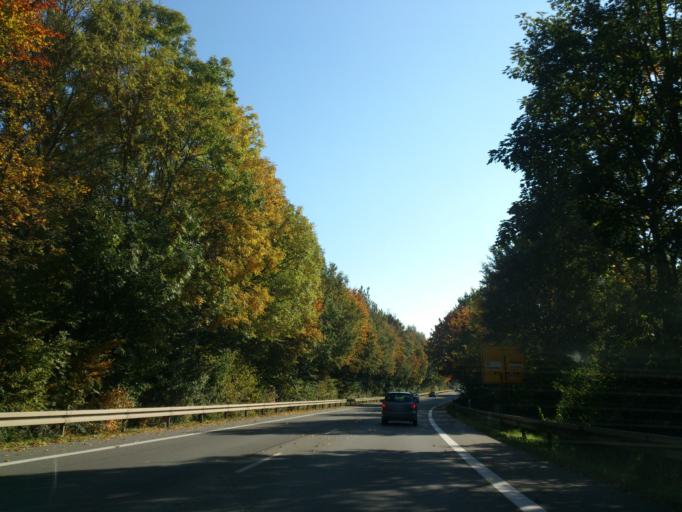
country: DE
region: North Rhine-Westphalia
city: Warburg
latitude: 51.4931
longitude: 9.1424
